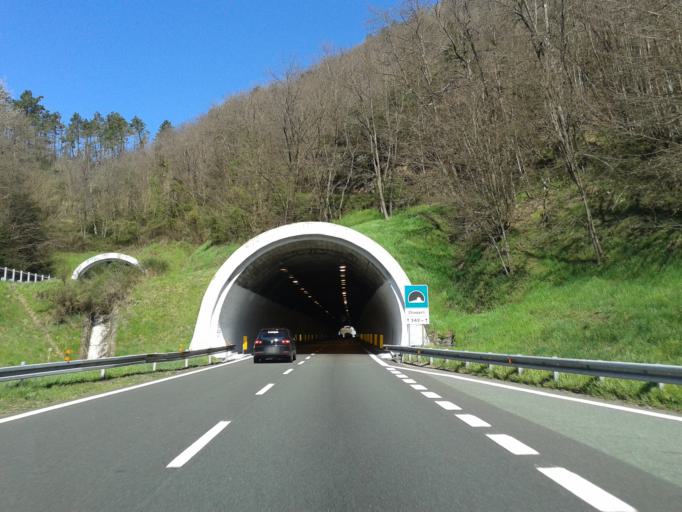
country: IT
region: Liguria
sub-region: Provincia di La Spezia
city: Bonassola
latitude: 44.2329
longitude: 9.6032
